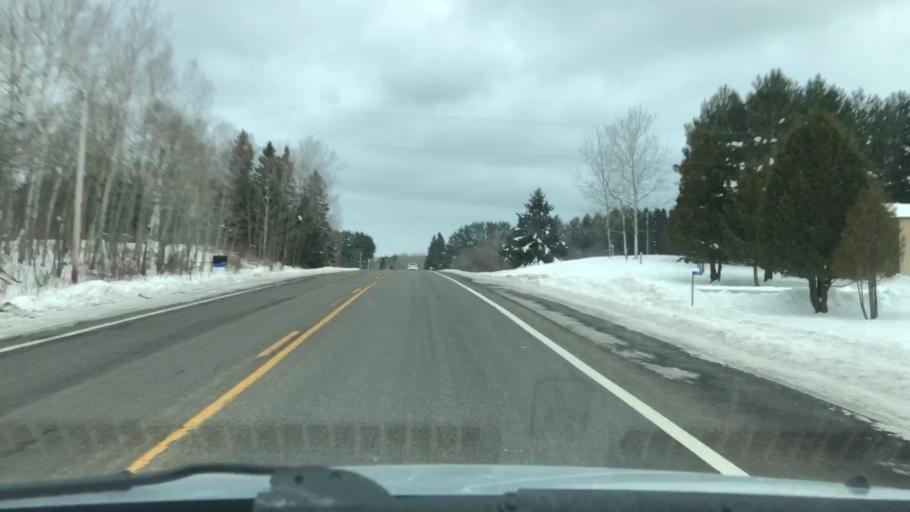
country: US
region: Minnesota
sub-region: Carlton County
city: Esko
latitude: 46.6809
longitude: -92.3706
